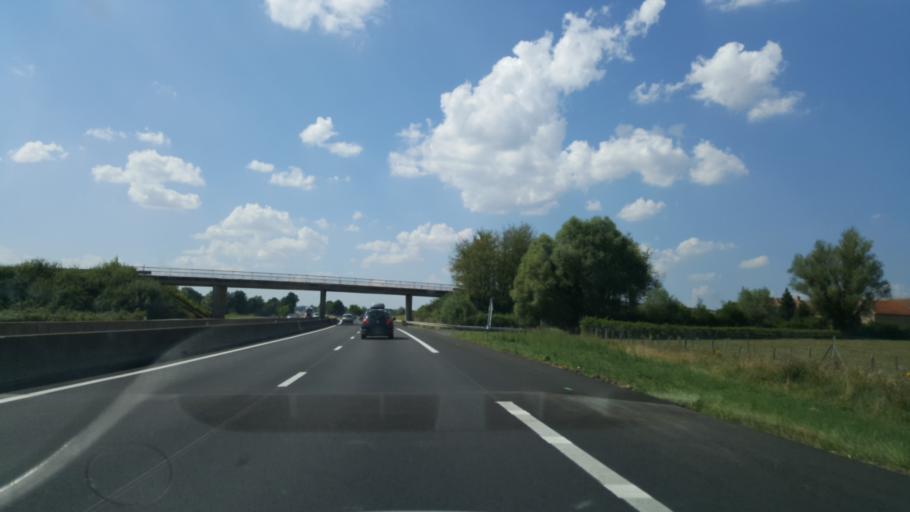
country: FR
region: Bourgogne
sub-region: Departement de la Cote-d'Or
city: Pouilly-en-Auxois
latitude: 47.2029
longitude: 4.6461
